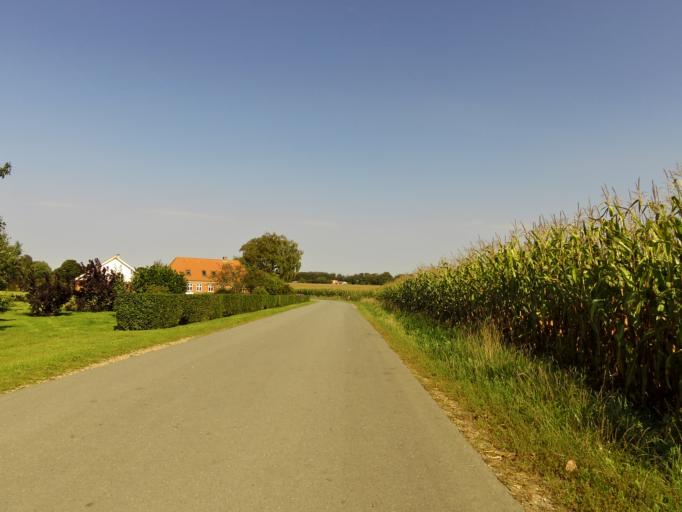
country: DK
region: South Denmark
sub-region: Vejen Kommune
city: Rodding
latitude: 55.3803
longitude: 9.1352
